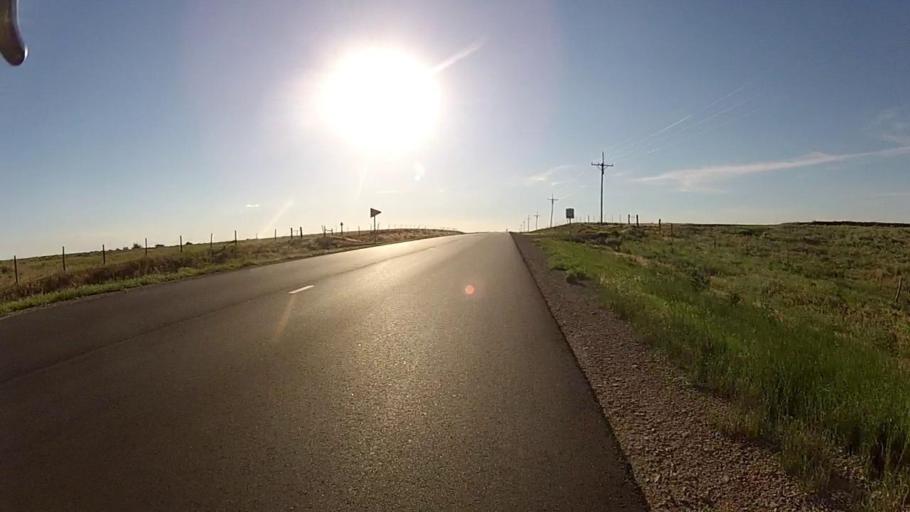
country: US
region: Kansas
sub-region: Comanche County
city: Coldwater
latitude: 37.2821
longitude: -99.1181
